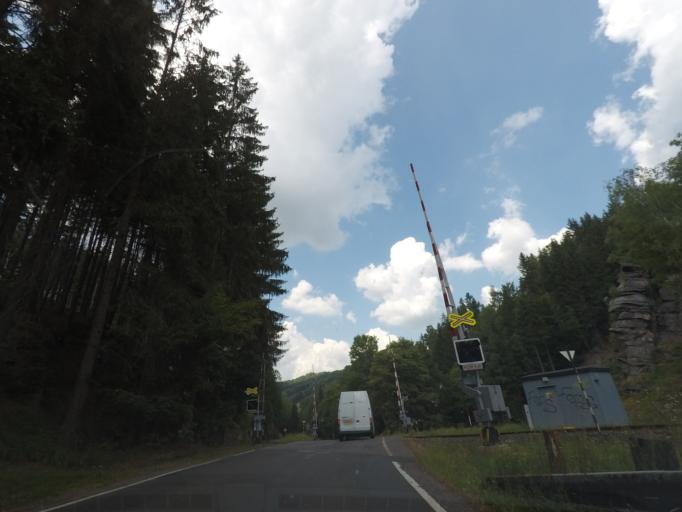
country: CZ
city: Radvanice
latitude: 50.6018
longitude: 16.0122
